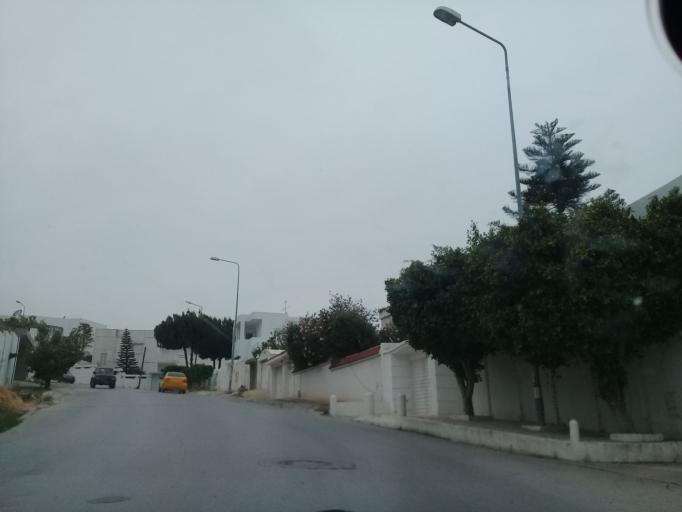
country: TN
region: Tunis
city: Tunis
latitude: 36.8431
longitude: 10.1497
